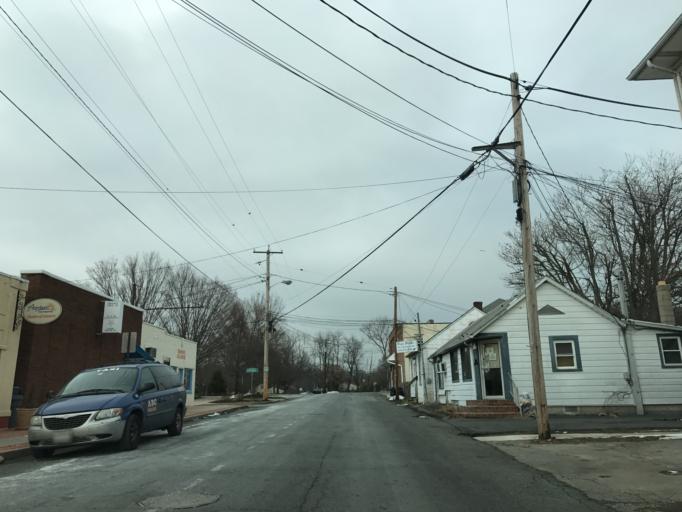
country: US
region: Maryland
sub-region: Harford County
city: Aberdeen
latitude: 39.5104
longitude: -76.1638
